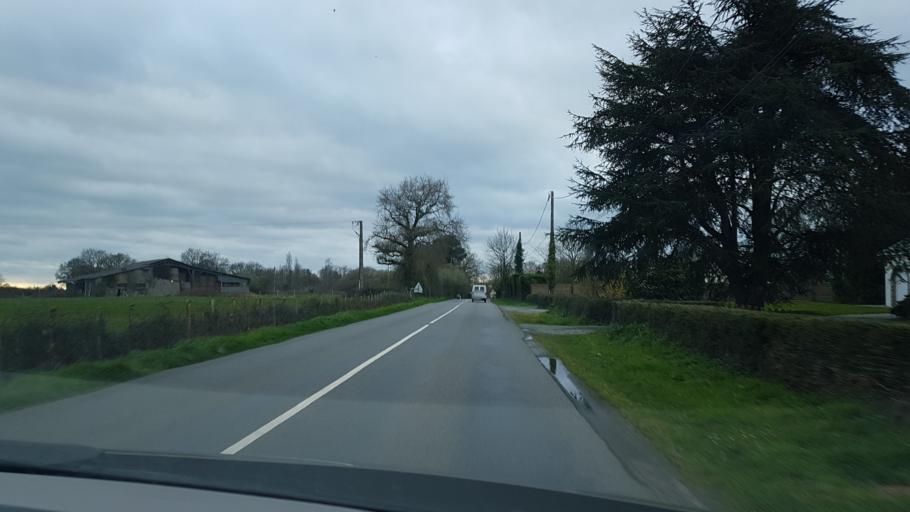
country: FR
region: Pays de la Loire
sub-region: Departement de la Loire-Atlantique
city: La Grigonnais
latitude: 47.5191
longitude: -1.6673
